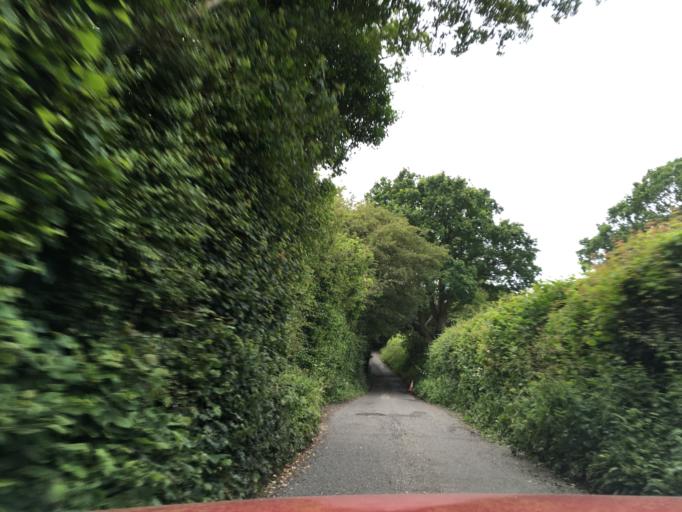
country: GB
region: England
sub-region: Bath and North East Somerset
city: Whitchurch
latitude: 51.4006
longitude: -2.5779
